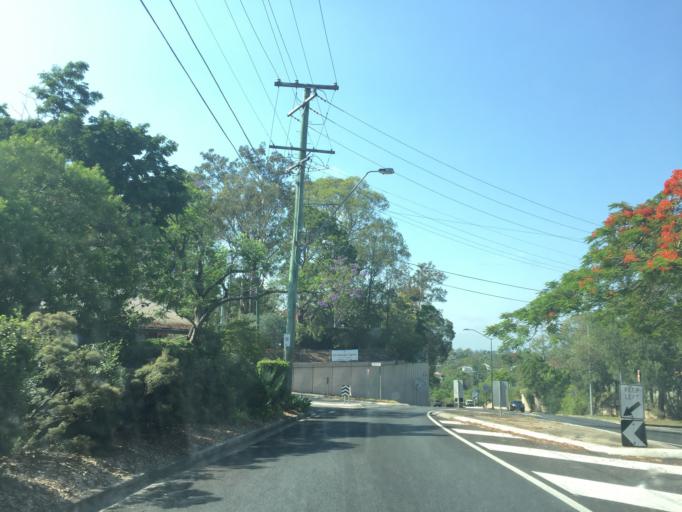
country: AU
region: Queensland
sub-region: Brisbane
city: Milton
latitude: -27.4602
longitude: 152.9885
